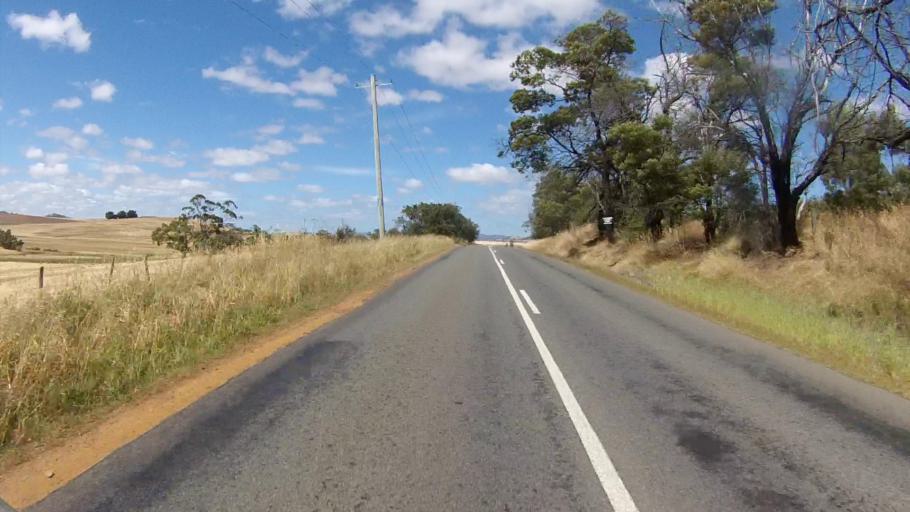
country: AU
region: Tasmania
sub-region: Clarence
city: Cambridge
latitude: -42.6524
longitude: 147.4336
